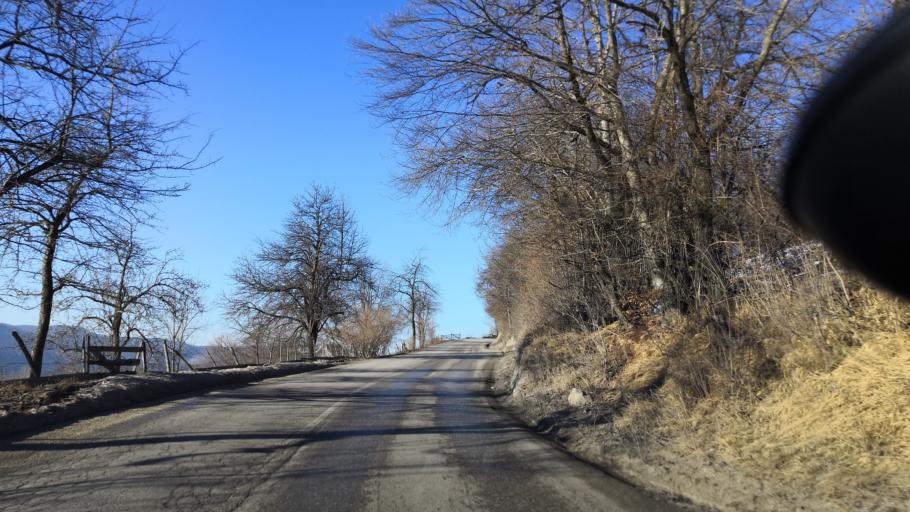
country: BA
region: Republika Srpska
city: Pale
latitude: 43.8971
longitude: 18.6361
